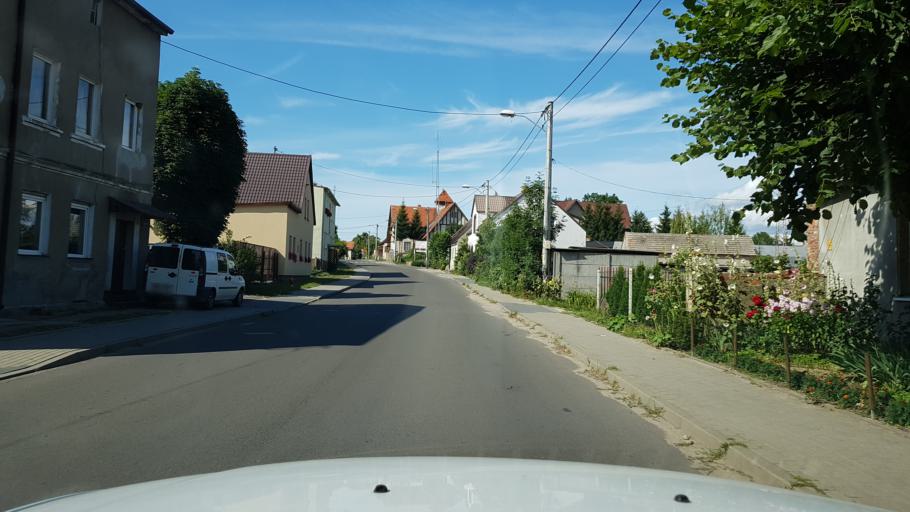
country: PL
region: West Pomeranian Voivodeship
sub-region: Powiat gryfinski
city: Stare Czarnowo
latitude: 53.2824
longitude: 14.7814
